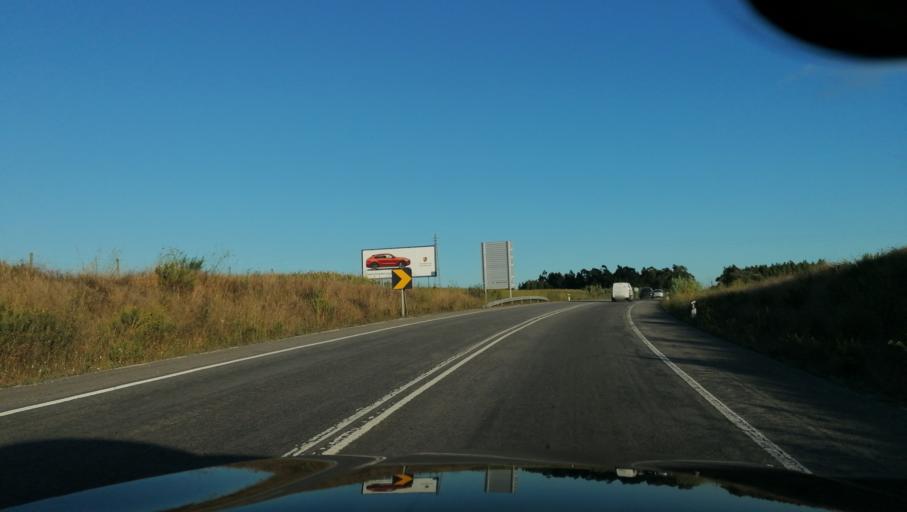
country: PT
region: Aveiro
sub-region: Aveiro
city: Aradas
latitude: 40.6099
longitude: -8.6253
